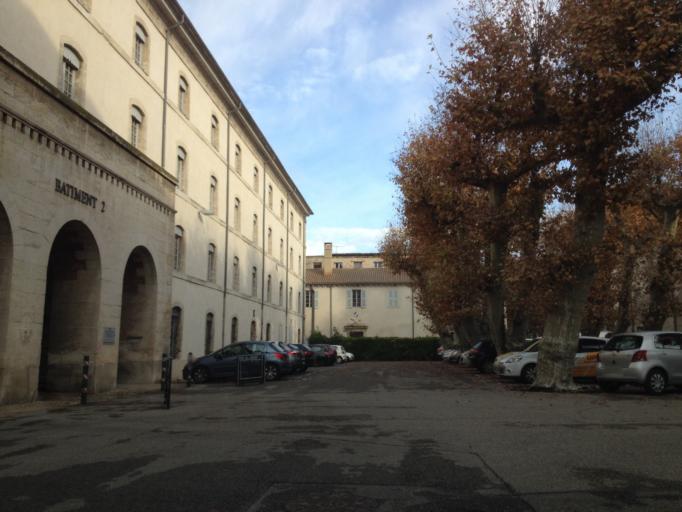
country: FR
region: Provence-Alpes-Cote d'Azur
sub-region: Departement du Vaucluse
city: Avignon
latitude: 43.9430
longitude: 4.8072
